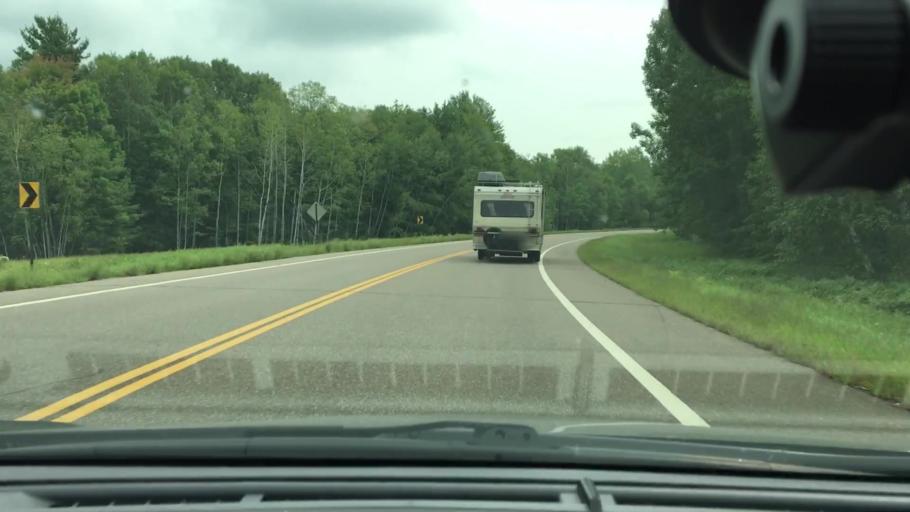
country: US
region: Minnesota
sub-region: Crow Wing County
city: Crosby
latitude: 46.4118
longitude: -93.8277
